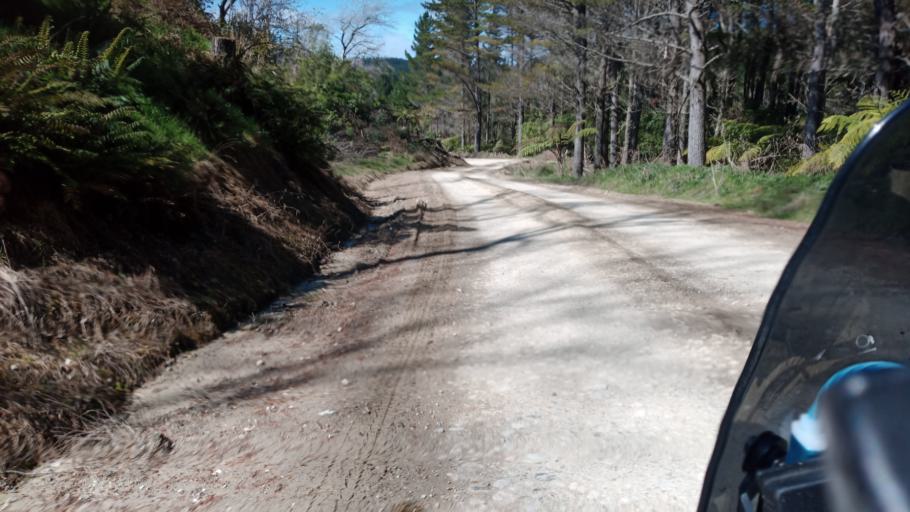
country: NZ
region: Gisborne
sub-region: Gisborne District
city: Gisborne
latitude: -38.8919
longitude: 177.7929
